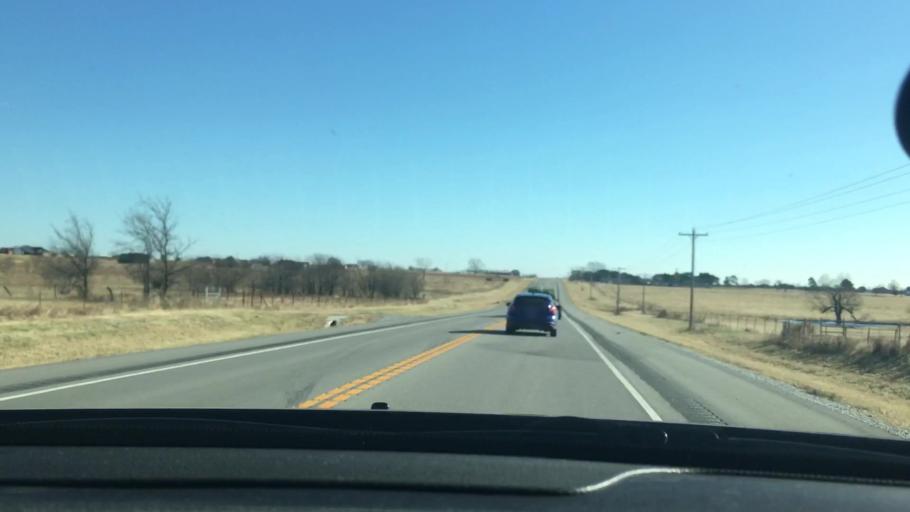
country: US
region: Oklahoma
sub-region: Love County
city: Marietta
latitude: 33.9404
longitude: -97.1701
